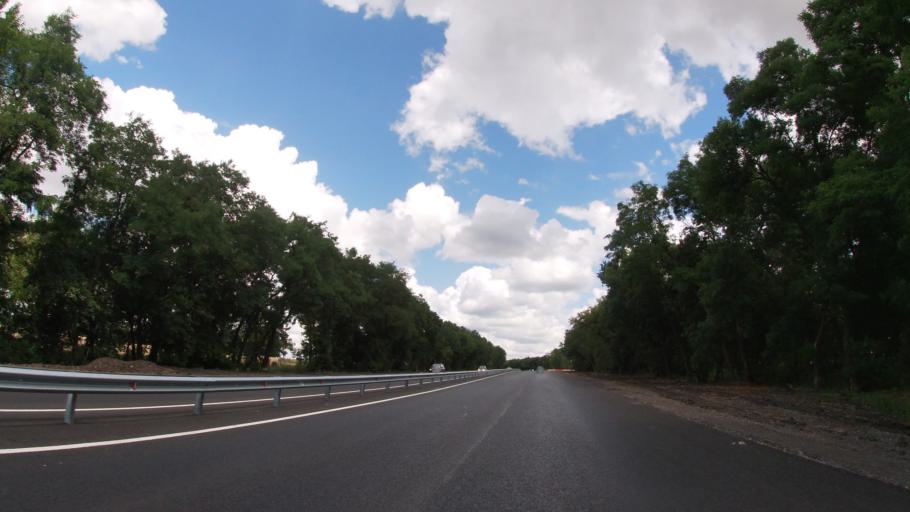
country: RU
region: Belgorod
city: Mayskiy
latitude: 50.4460
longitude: 36.3982
